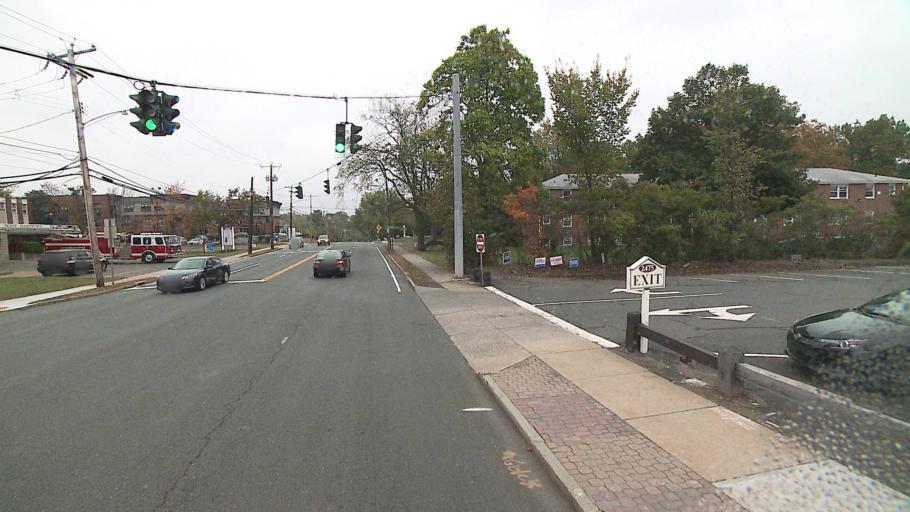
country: US
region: Connecticut
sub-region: Hartford County
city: West Hartford
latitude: 41.7861
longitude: -72.7446
